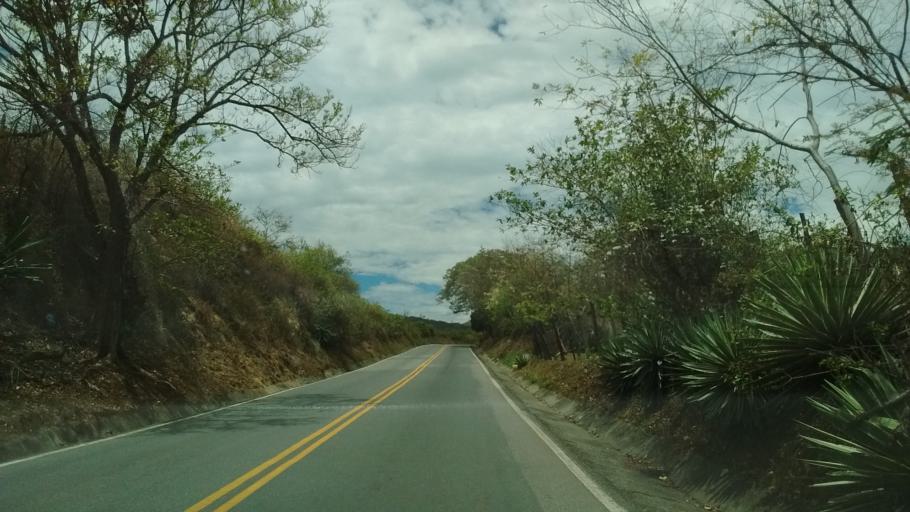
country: CO
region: Cauca
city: La Sierra
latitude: 2.2182
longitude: -76.7996
